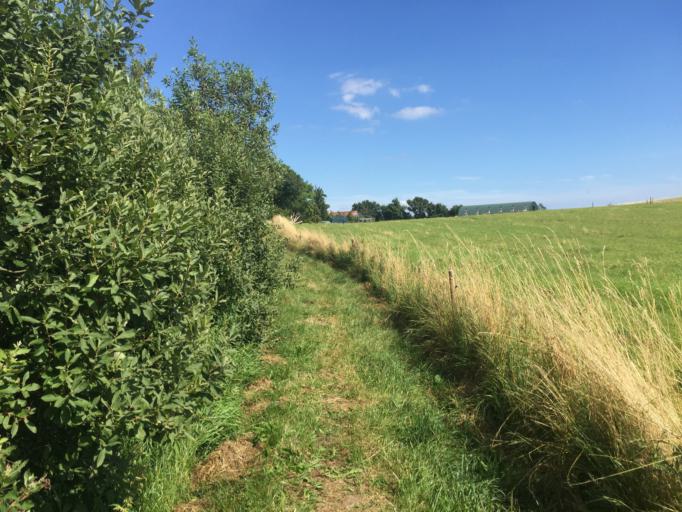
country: DK
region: South Denmark
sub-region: Faaborg-Midtfyn Kommune
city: Faaborg
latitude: 55.0660
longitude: 10.2397
